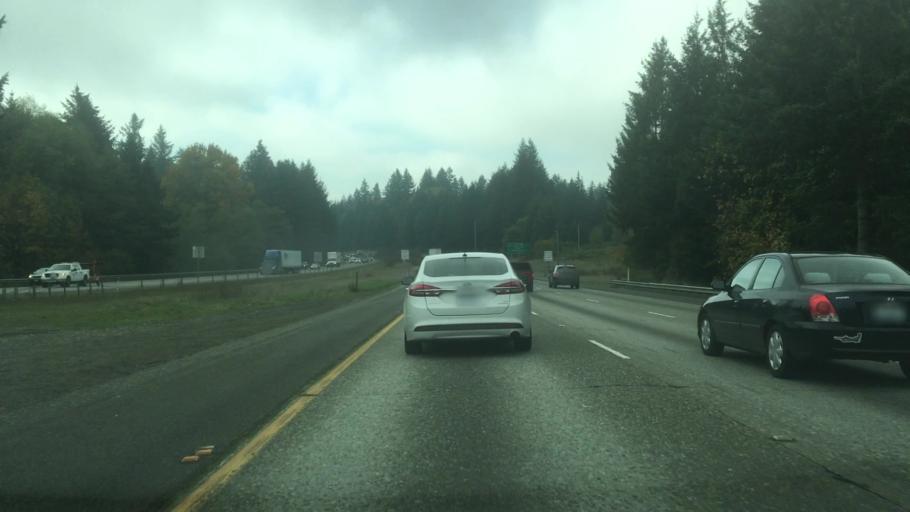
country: US
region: Washington
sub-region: Thurston County
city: Tanglewilde-Thompson Place
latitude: 47.0577
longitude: -122.8017
